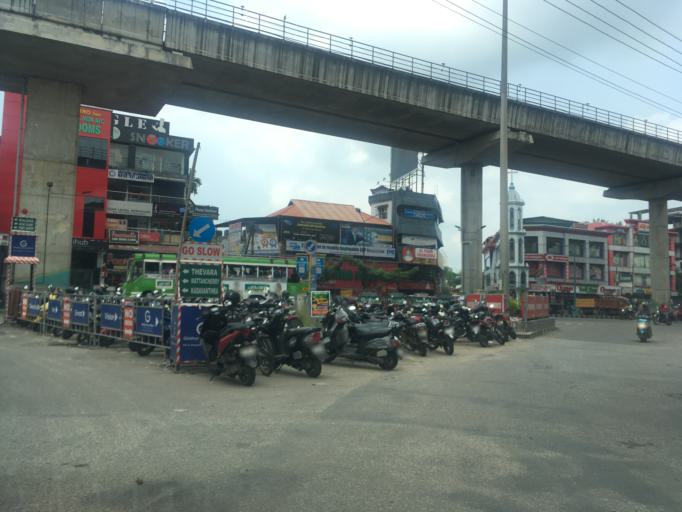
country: IN
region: Kerala
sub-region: Ernakulam
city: Elur
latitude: 10.0287
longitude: 76.3107
